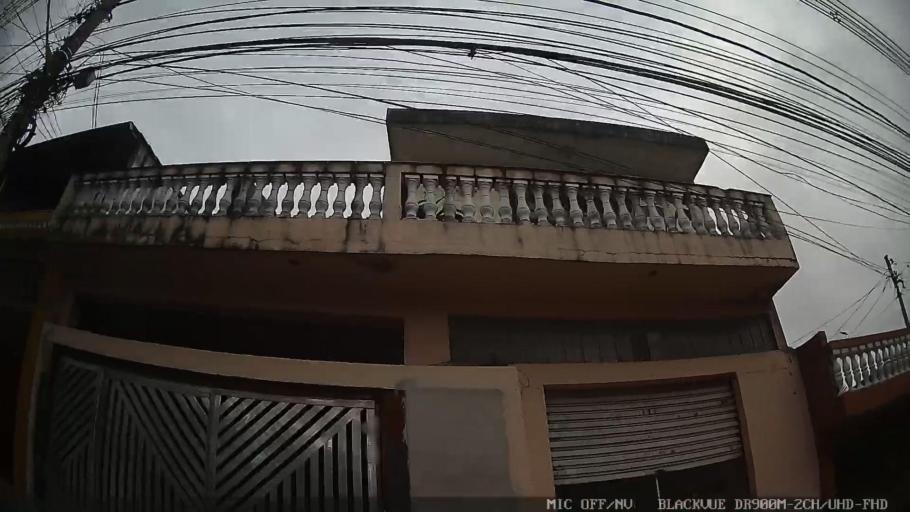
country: BR
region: Sao Paulo
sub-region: Osasco
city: Osasco
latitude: -23.4949
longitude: -46.7974
